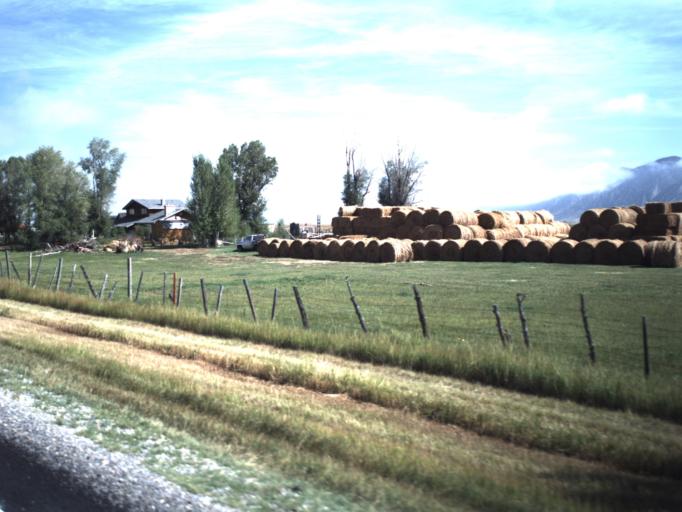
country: US
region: Utah
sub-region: Rich County
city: Randolph
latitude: 41.6218
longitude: -111.1792
